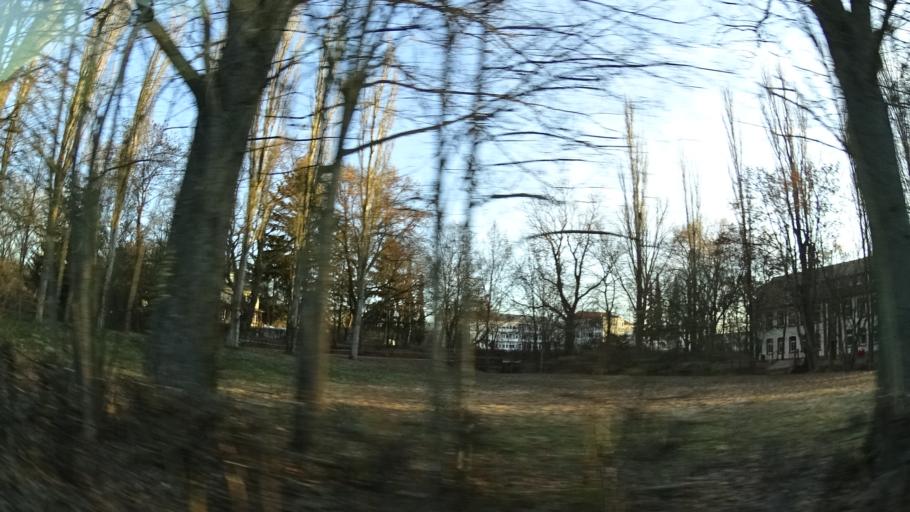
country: DE
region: Rheinland-Pfalz
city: Marnheim
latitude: 49.6345
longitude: 8.0262
